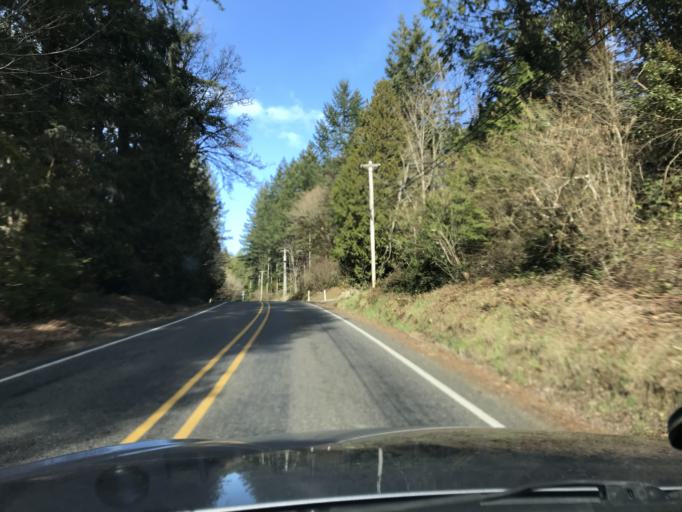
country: US
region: Washington
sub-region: Pierce County
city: Home
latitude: 47.2467
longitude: -122.7749
